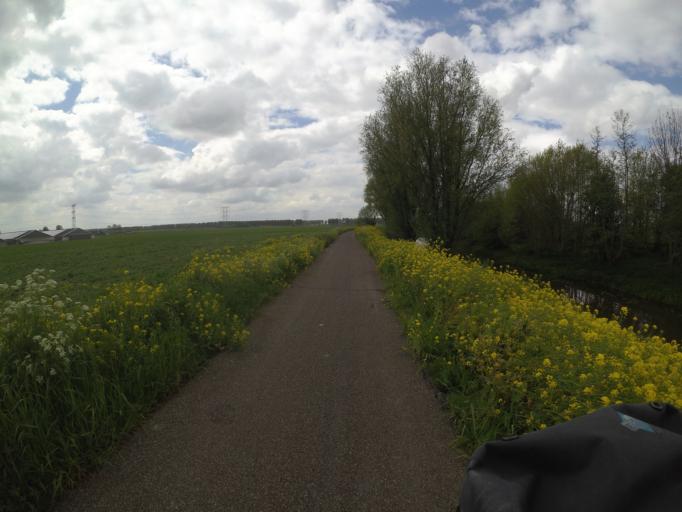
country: NL
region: North Brabant
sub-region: Gemeente Geertruidenberg
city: Geertruidenberg
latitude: 51.6789
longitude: 4.8962
